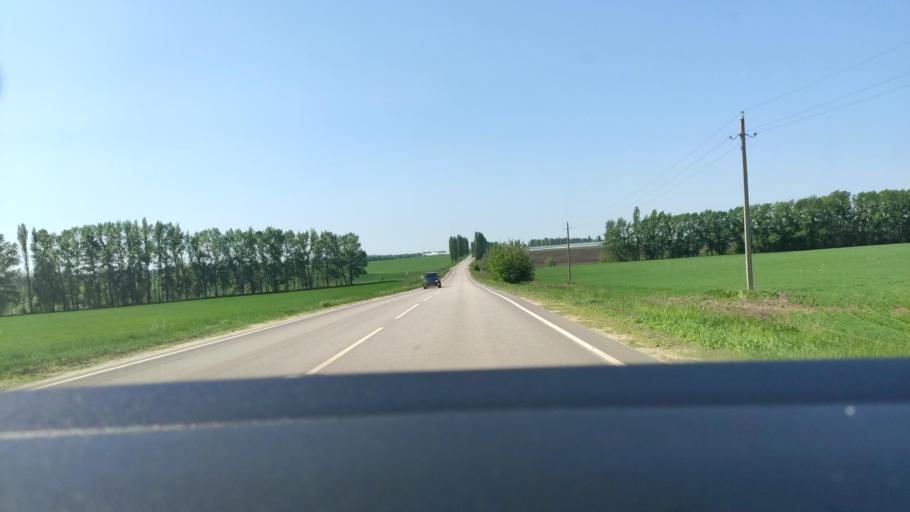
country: RU
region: Voronezj
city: Novaya Usman'
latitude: 51.5543
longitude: 39.3737
